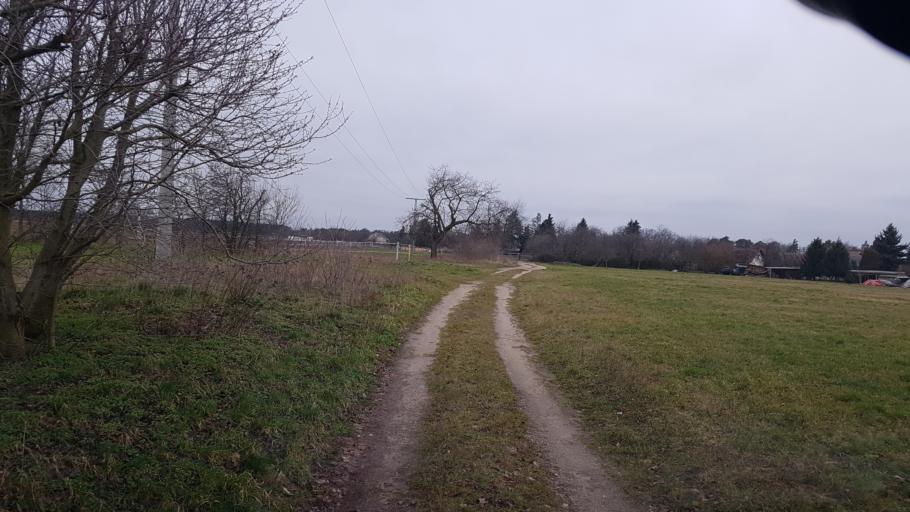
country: DE
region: Brandenburg
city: Crinitz
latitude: 51.7374
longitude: 13.7217
